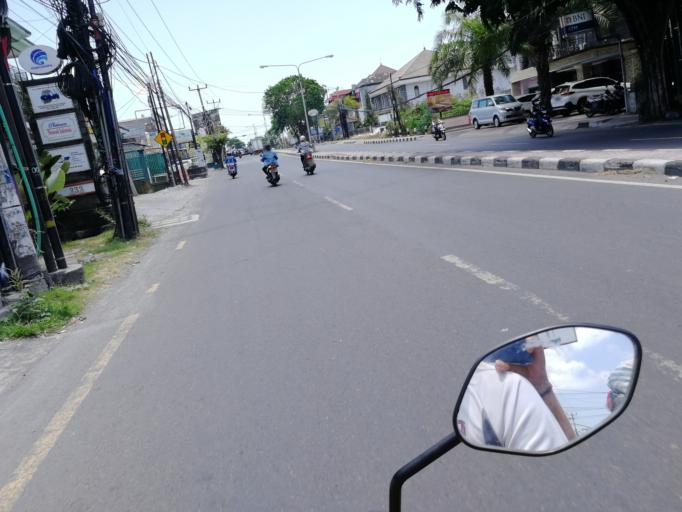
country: ID
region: Bali
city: Banjar Kertasari
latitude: -8.6368
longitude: 115.1832
